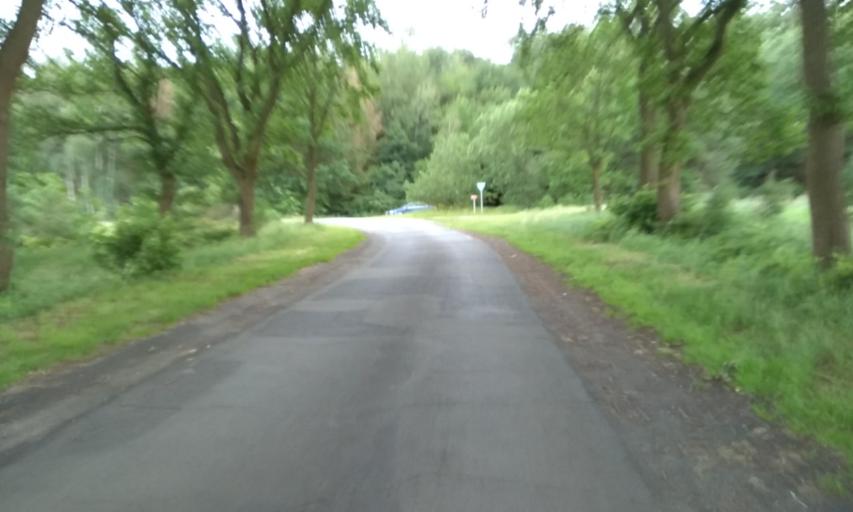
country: DE
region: Lower Saxony
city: Sauensiek
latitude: 53.3849
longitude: 9.6155
